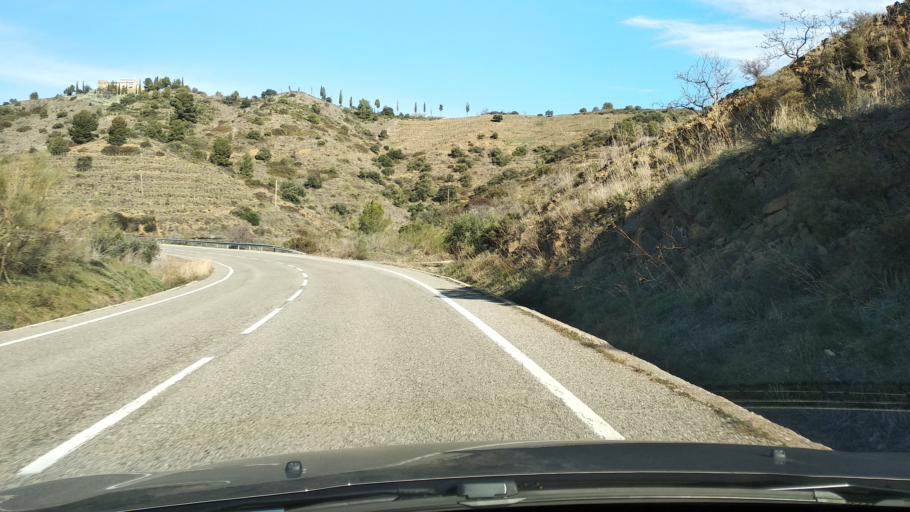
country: ES
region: Catalonia
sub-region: Provincia de Tarragona
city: Falset
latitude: 41.2032
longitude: 0.7813
